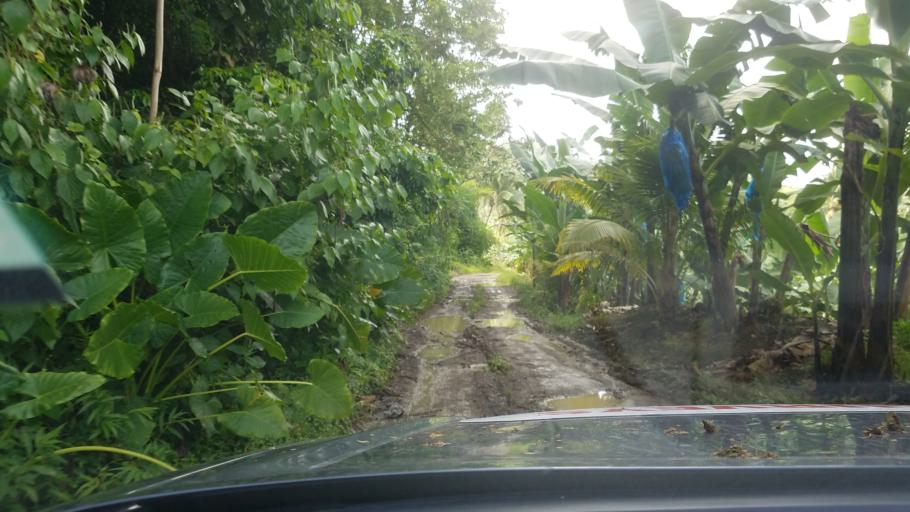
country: LC
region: Anse-la-Raye
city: Anse La Raye
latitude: 13.9386
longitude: -60.9905
